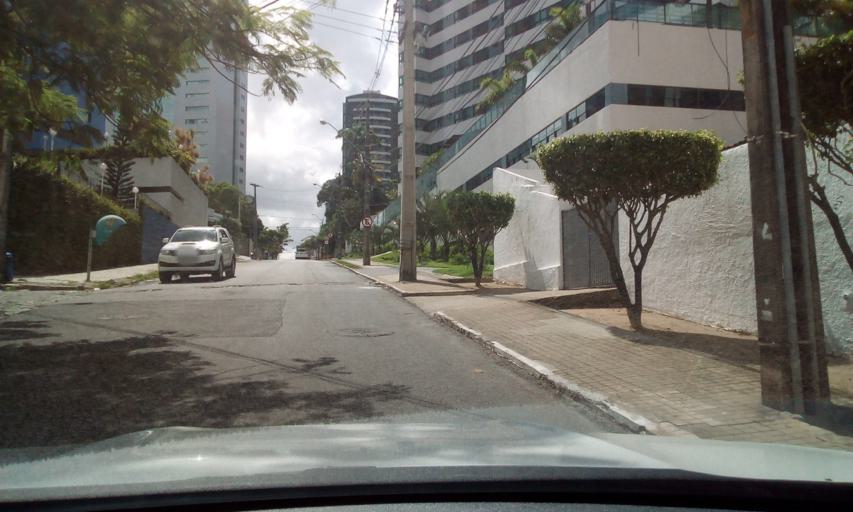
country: BR
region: Paraiba
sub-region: Joao Pessoa
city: Joao Pessoa
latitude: -7.1170
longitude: -34.8350
